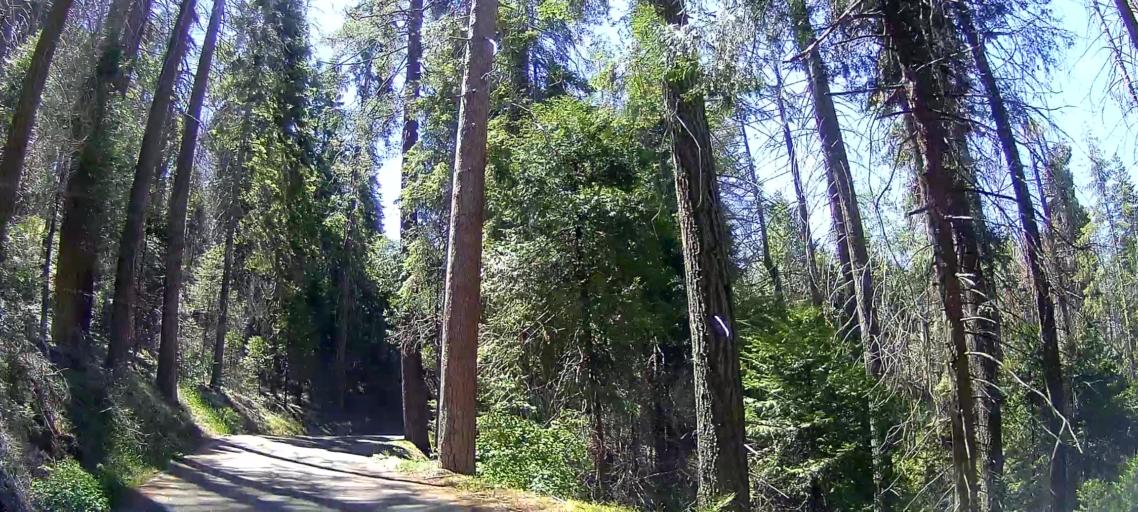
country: US
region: California
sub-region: Tulare County
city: Three Rivers
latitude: 36.5617
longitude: -118.7850
